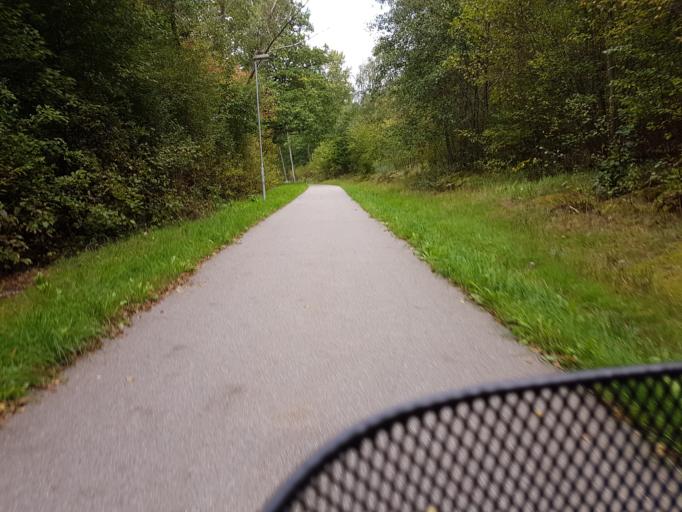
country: SE
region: Vaestra Goetaland
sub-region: Ale Kommun
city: Nodinge-Nol
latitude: 57.9026
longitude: 12.0595
